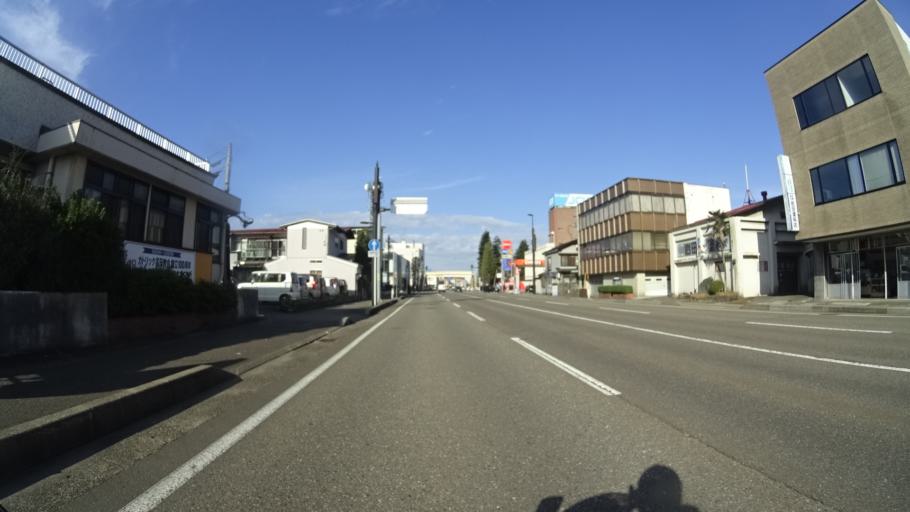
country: JP
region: Niigata
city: Joetsu
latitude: 37.1118
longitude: 138.2506
